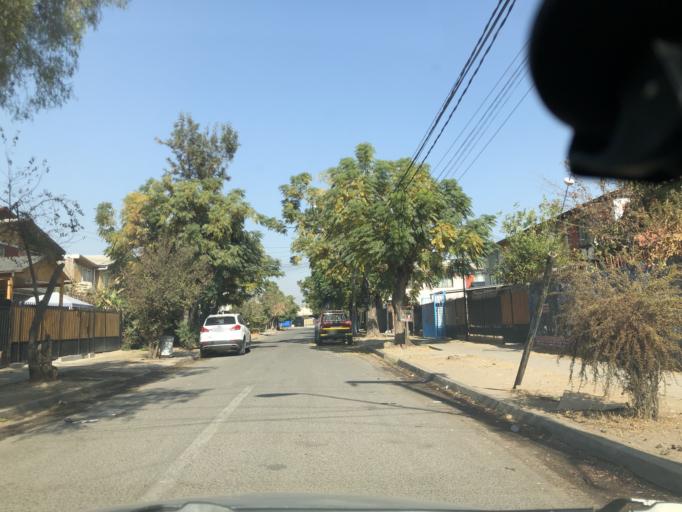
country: CL
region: Santiago Metropolitan
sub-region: Provincia de Cordillera
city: Puente Alto
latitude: -33.5933
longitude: -70.5709
